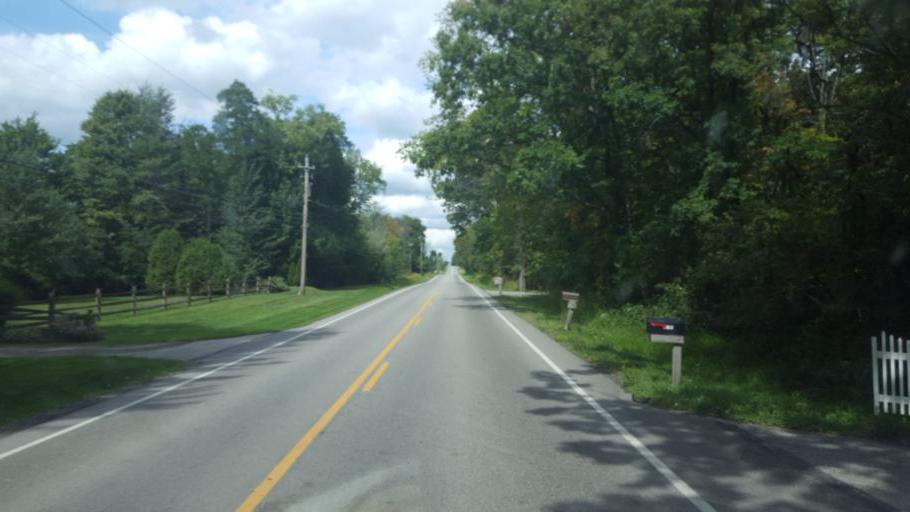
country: US
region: Ohio
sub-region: Geauga County
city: Middlefield
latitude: 41.4127
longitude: -81.0333
